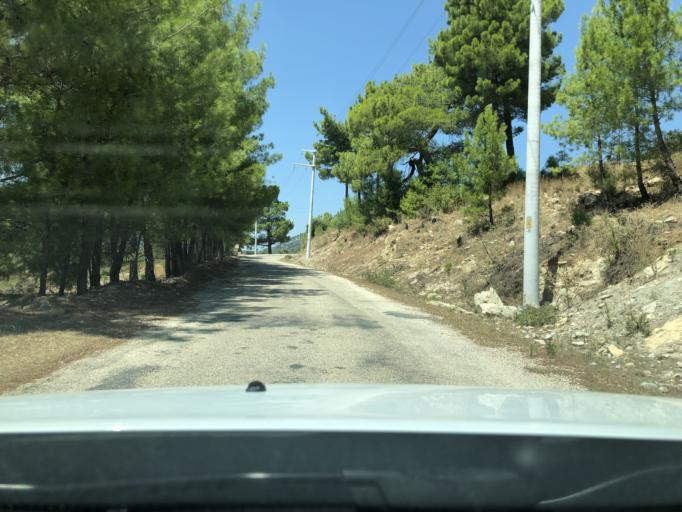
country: TR
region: Antalya
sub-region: Manavgat
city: Manavgat
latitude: 36.8809
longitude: 31.5502
